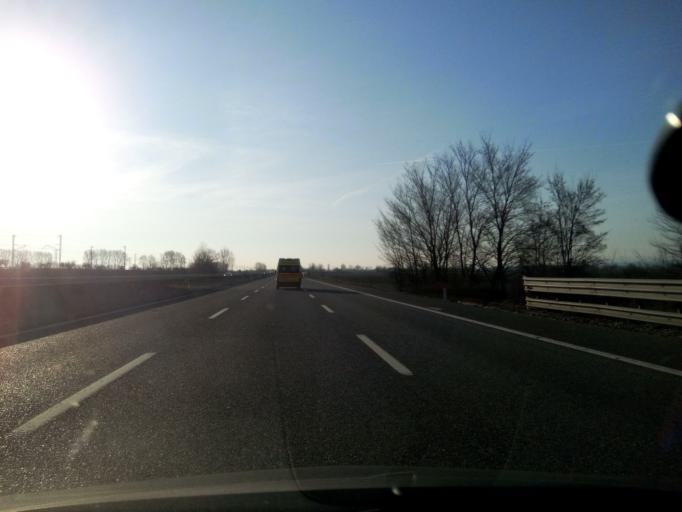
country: IT
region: Emilia-Romagna
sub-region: Provincia di Piacenza
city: Alseno
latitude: 44.9292
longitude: 9.9807
